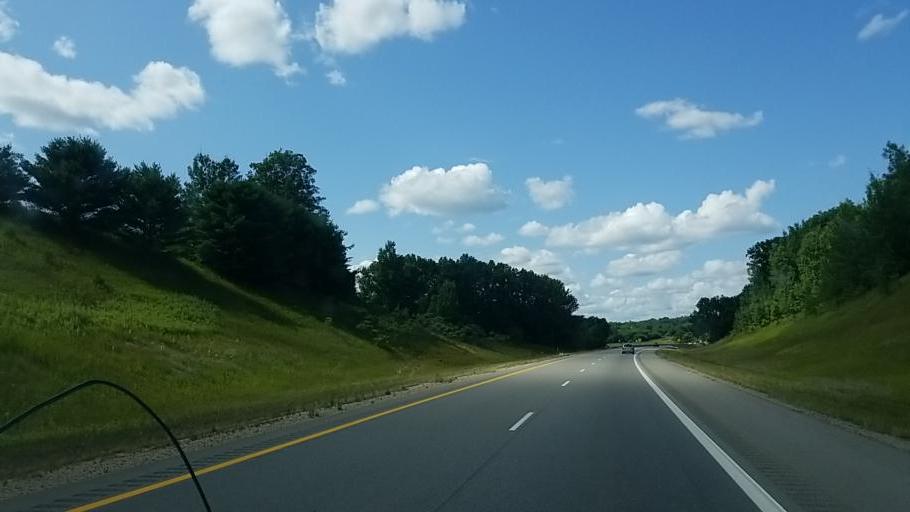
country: US
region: Michigan
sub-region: Mecosta County
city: Big Rapids
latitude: 43.6522
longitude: -85.5176
